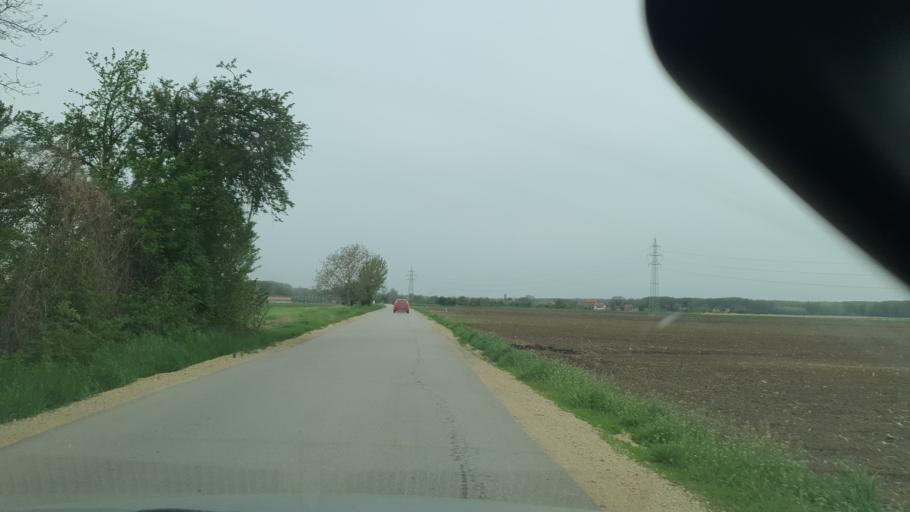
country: RS
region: Central Serbia
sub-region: Branicevski Okrug
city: Pozarevac
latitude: 44.7127
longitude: 21.1316
